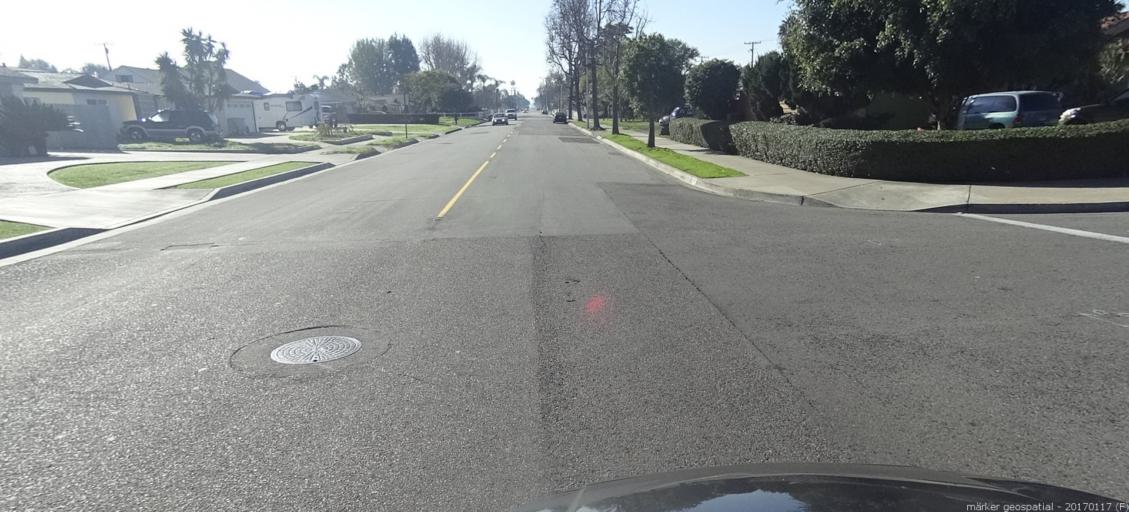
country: US
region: California
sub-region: Orange County
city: Stanton
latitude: 33.8282
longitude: -117.9677
